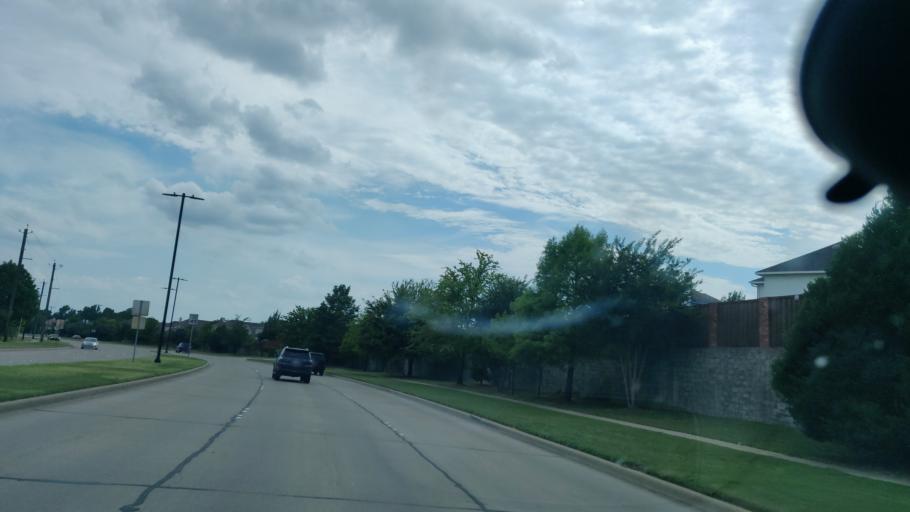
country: US
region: Texas
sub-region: Dallas County
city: Rowlett
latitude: 32.9312
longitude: -96.5975
